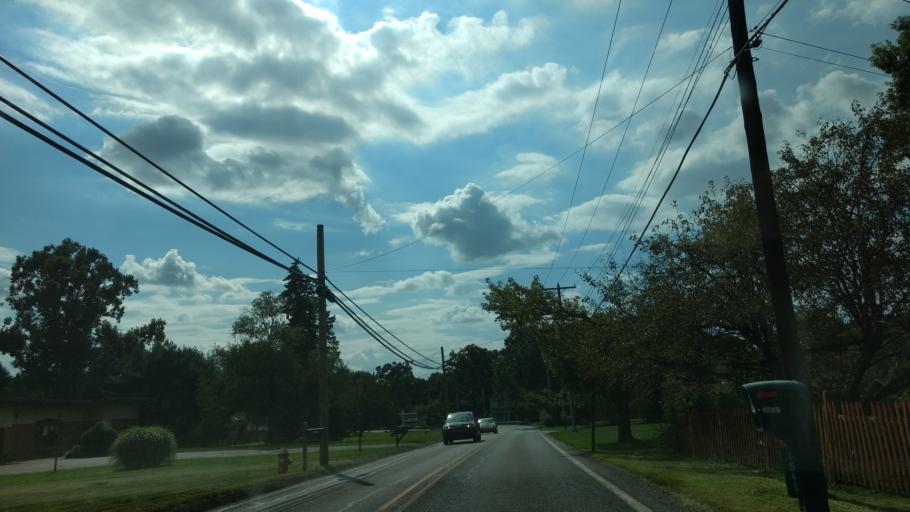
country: US
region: Pennsylvania
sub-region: Allegheny County
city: Franklin Park
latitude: 40.5851
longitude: -80.0767
